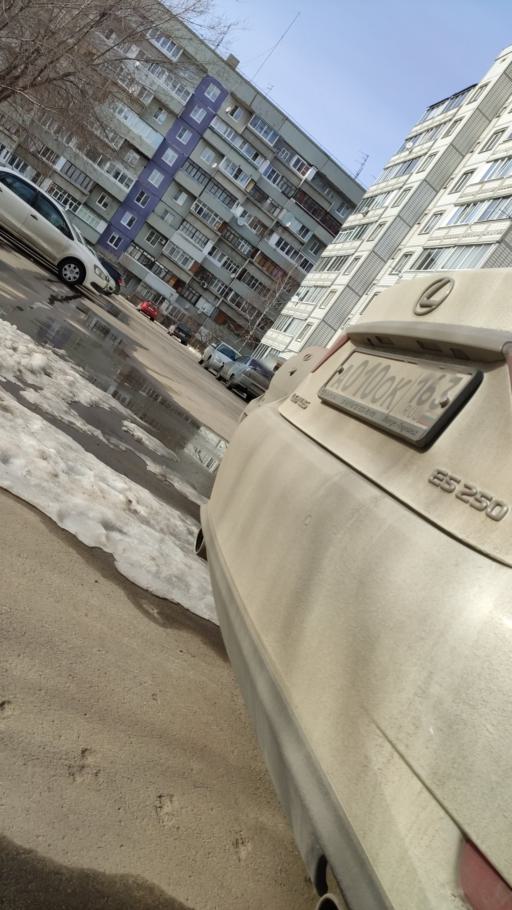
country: RU
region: Samara
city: Povolzhskiy
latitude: 53.5861
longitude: 49.7682
